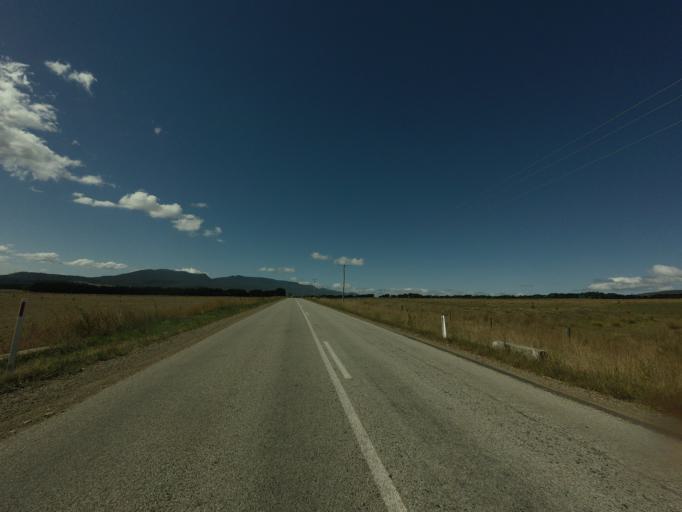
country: AU
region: Tasmania
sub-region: Break O'Day
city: St Helens
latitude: -41.6108
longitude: 148.0184
